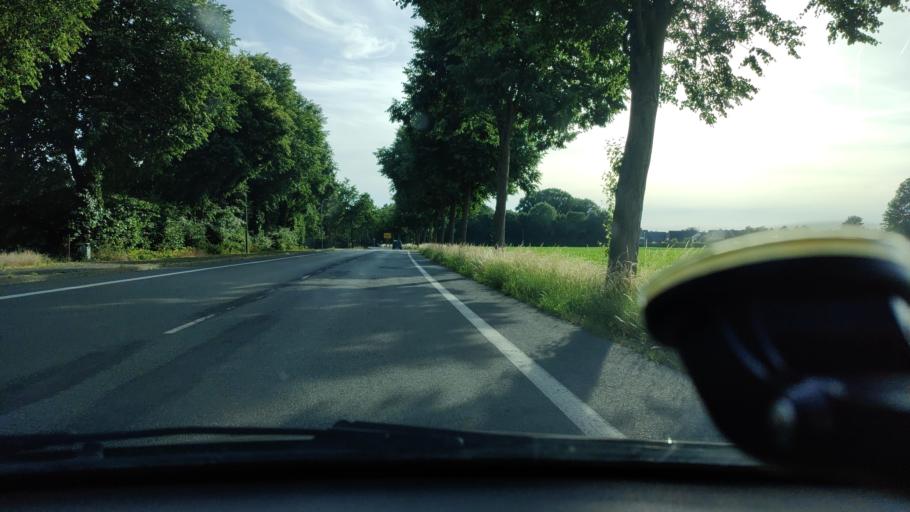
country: DE
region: North Rhine-Westphalia
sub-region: Regierungsbezirk Munster
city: Schoppingen
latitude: 52.0191
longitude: 7.2185
